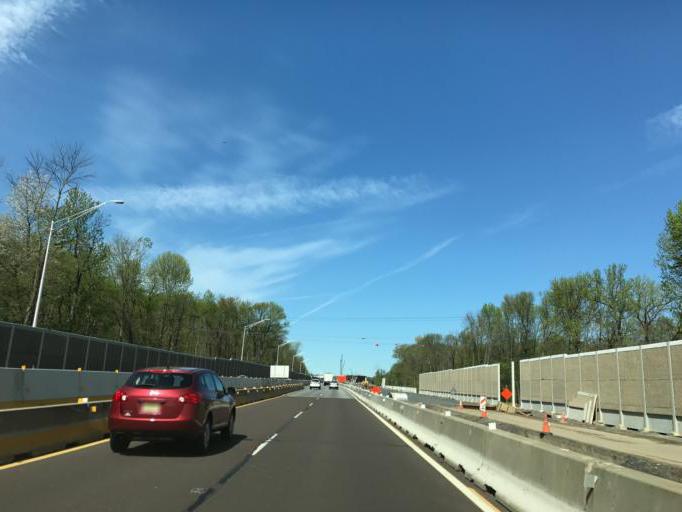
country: US
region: Pennsylvania
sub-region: Bucks County
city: Bristol
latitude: 40.1258
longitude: -74.8682
